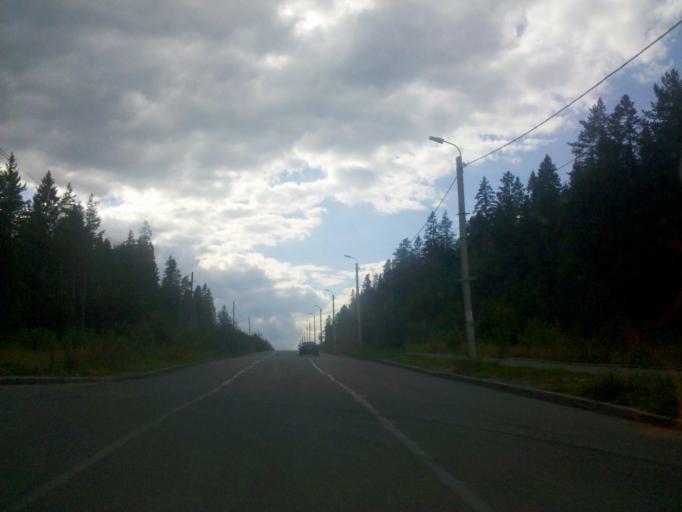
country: RU
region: Republic of Karelia
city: Petrozavodsk
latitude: 61.7777
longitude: 34.3059
